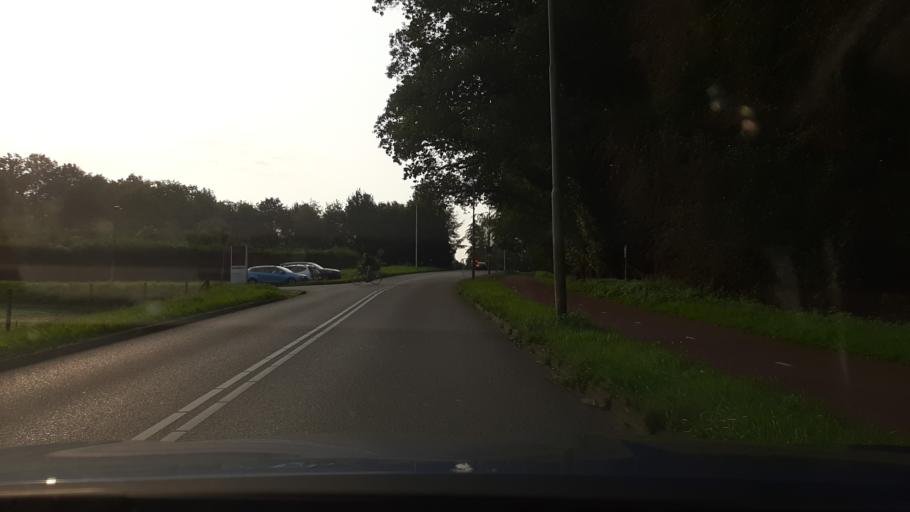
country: NL
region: Gelderland
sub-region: Gemeente Arnhem
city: Burgemeesterswijk
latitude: 51.9959
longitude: 5.9088
